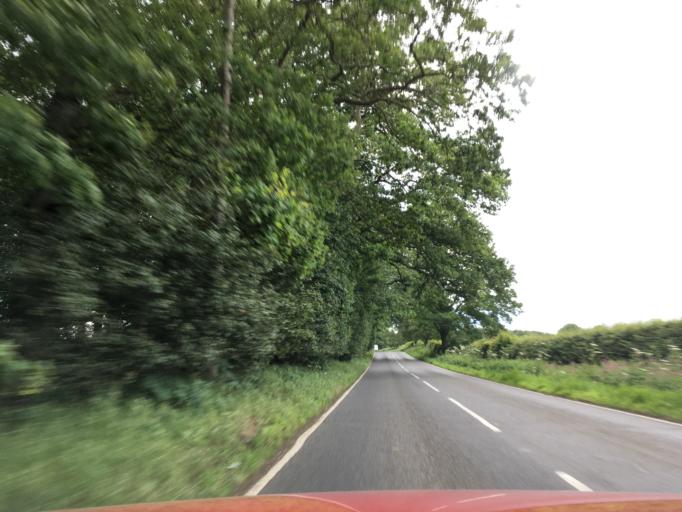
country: GB
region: England
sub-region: Central Bedfordshire
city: Woburn
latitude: 51.9731
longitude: -0.6415
